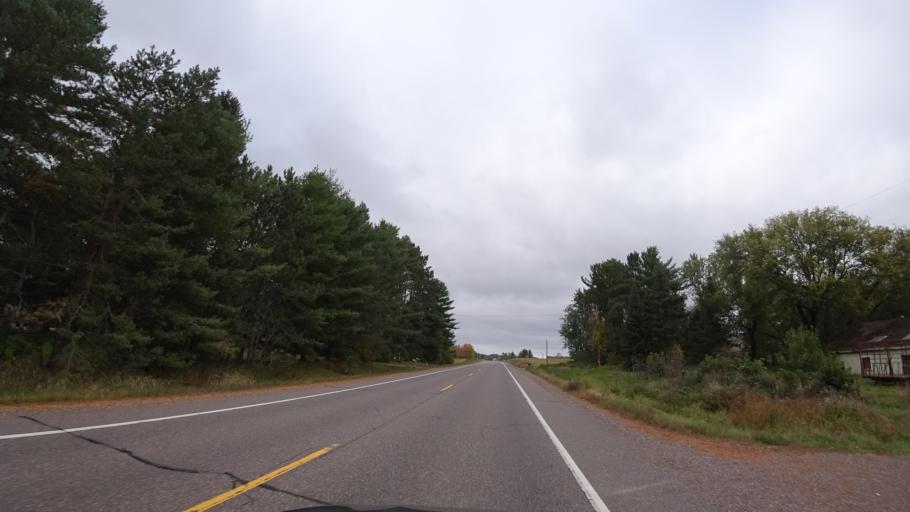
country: US
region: Wisconsin
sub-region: Rusk County
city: Ladysmith
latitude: 45.5415
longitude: -91.1114
